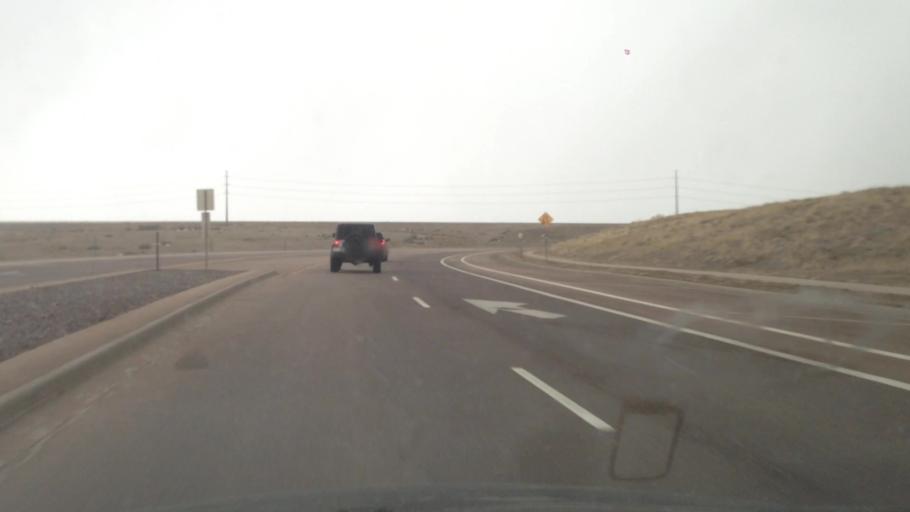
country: US
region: Colorado
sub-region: Douglas County
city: Stonegate
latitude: 39.4921
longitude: -104.8069
